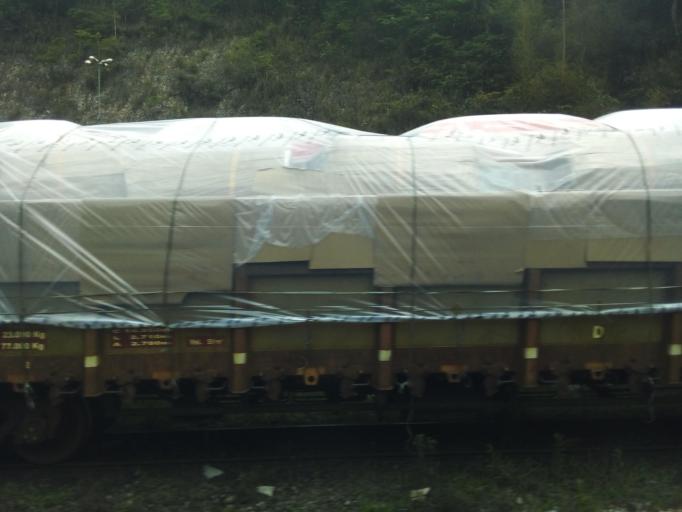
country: BR
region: Minas Gerais
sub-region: Joao Monlevade
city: Joao Monlevade
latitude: -19.8417
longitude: -43.1285
